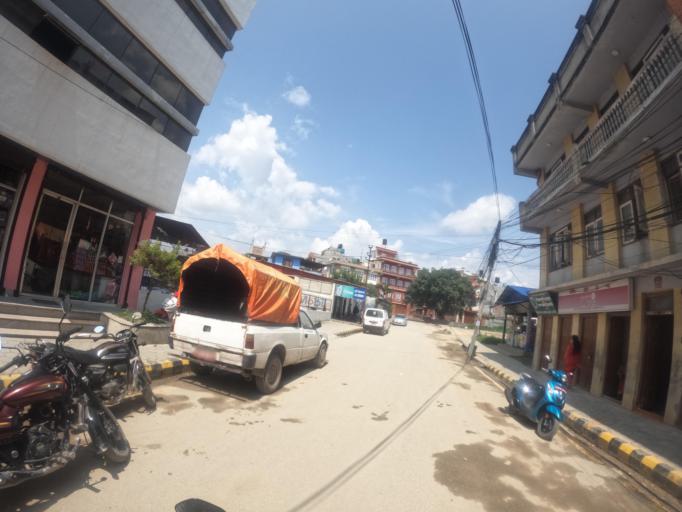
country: NP
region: Central Region
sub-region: Bagmati Zone
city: Bhaktapur
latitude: 27.6906
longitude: 85.3902
